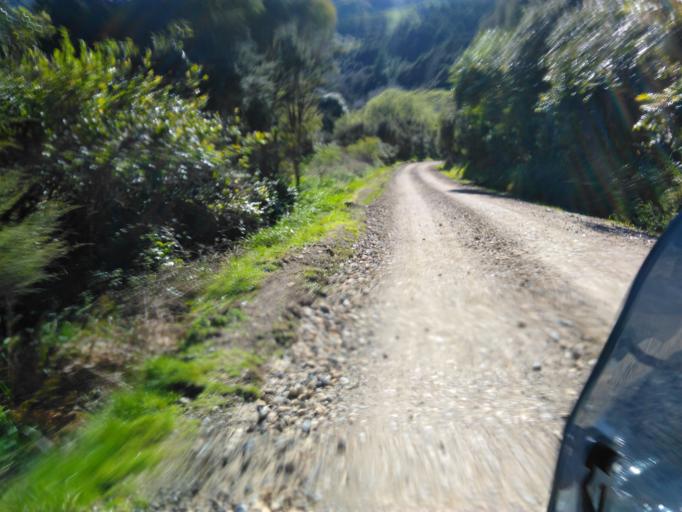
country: NZ
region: Gisborne
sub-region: Gisborne District
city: Gisborne
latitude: -38.3906
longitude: 177.6620
